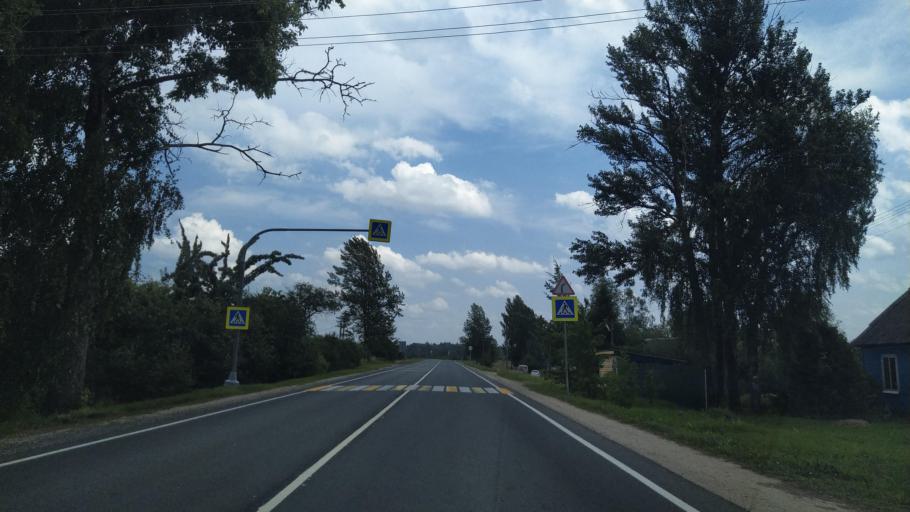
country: RU
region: Pskov
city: Pskov
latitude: 57.7557
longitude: 28.7720
